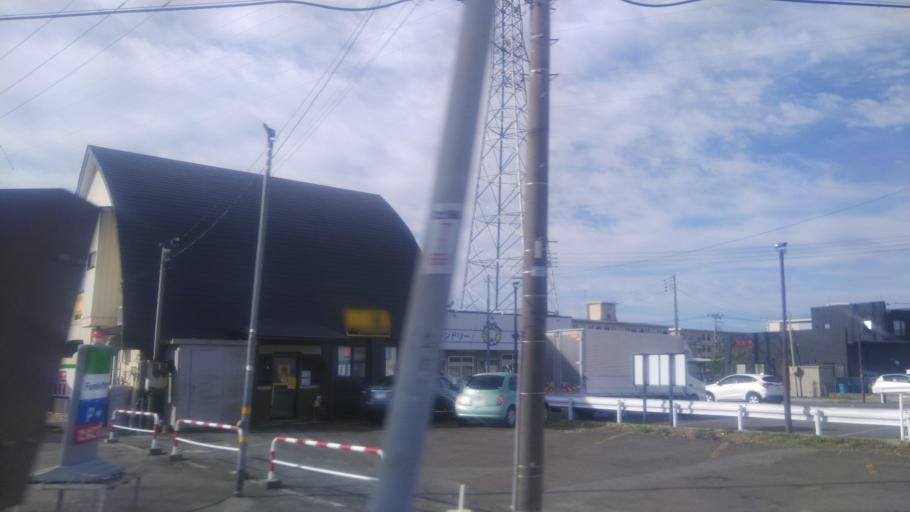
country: JP
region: Akita
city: Noshiromachi
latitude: 40.1908
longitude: 140.0361
